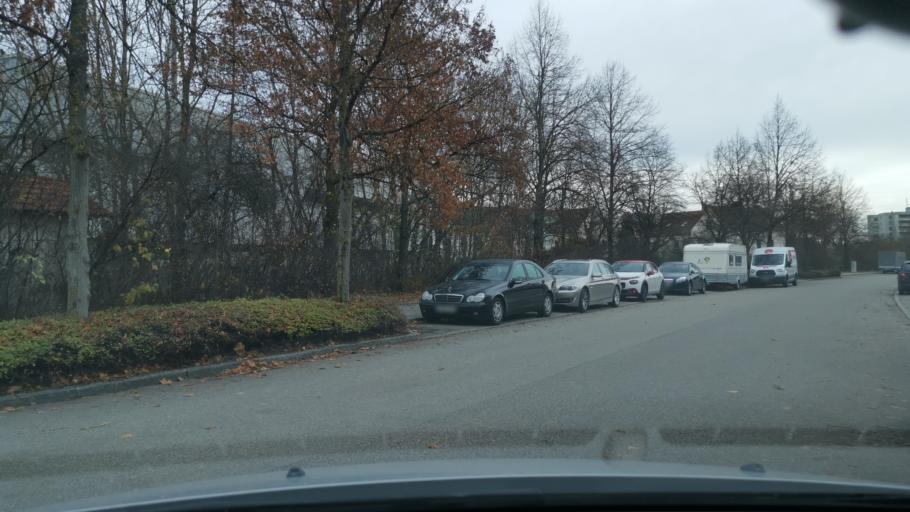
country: DE
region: Bavaria
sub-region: Upper Bavaria
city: Unterschleissheim
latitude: 48.2743
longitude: 11.5776
